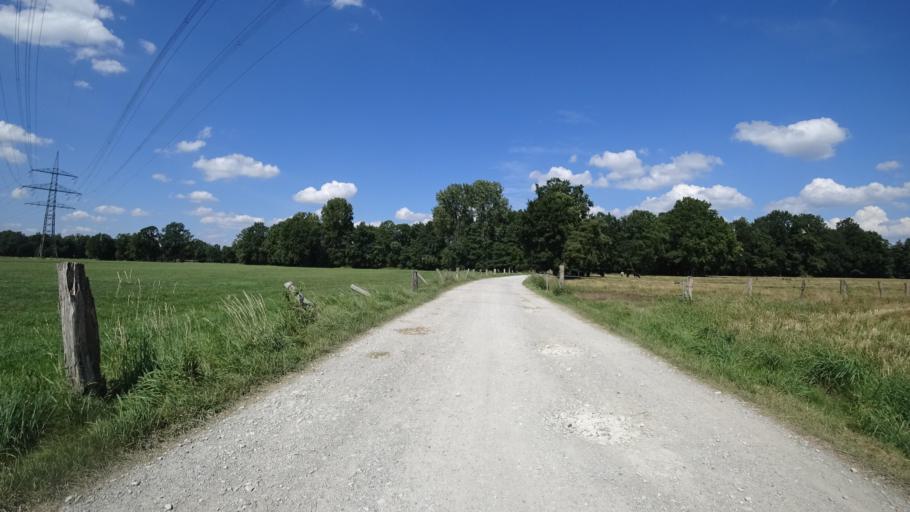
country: DE
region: North Rhine-Westphalia
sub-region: Regierungsbezirk Detmold
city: Guetersloh
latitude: 51.9318
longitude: 8.3980
